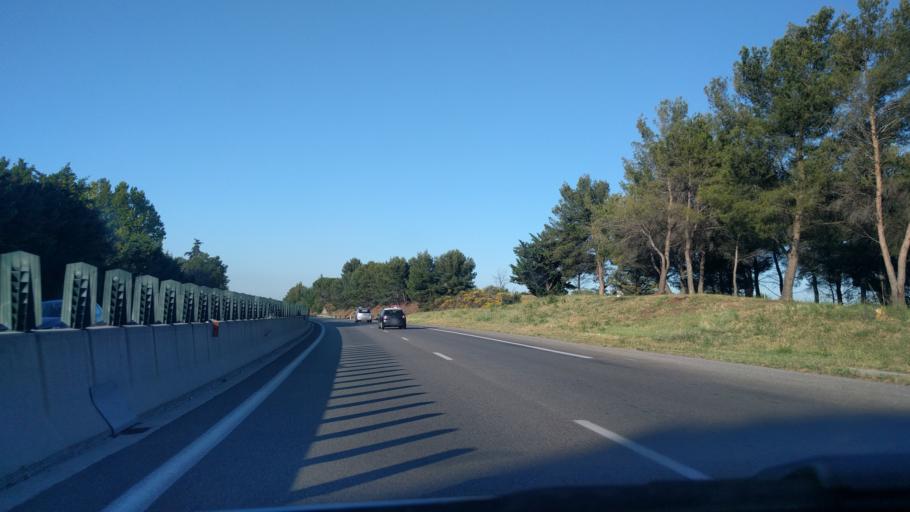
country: FR
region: Provence-Alpes-Cote d'Azur
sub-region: Departement des Bouches-du-Rhone
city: Venelles
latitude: 43.5726
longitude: 5.4685
